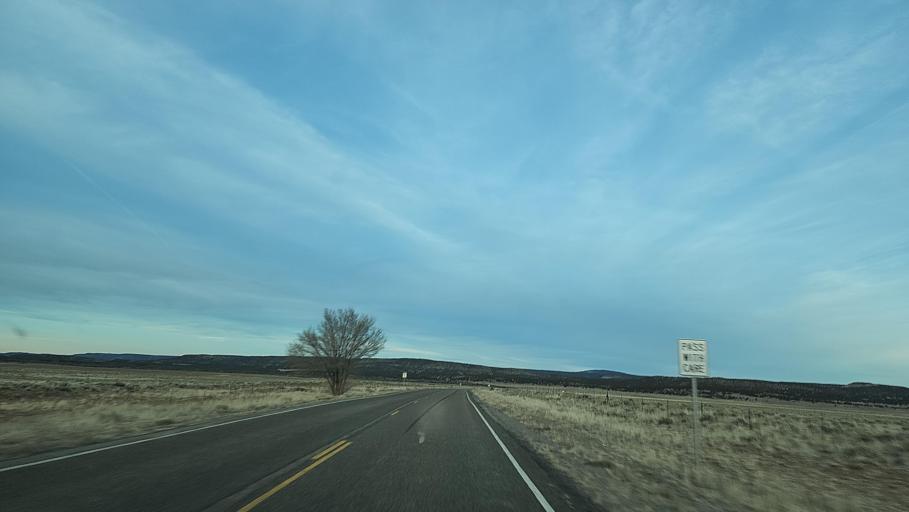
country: US
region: New Mexico
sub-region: Cibola County
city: Grants
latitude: 34.7081
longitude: -108.0106
